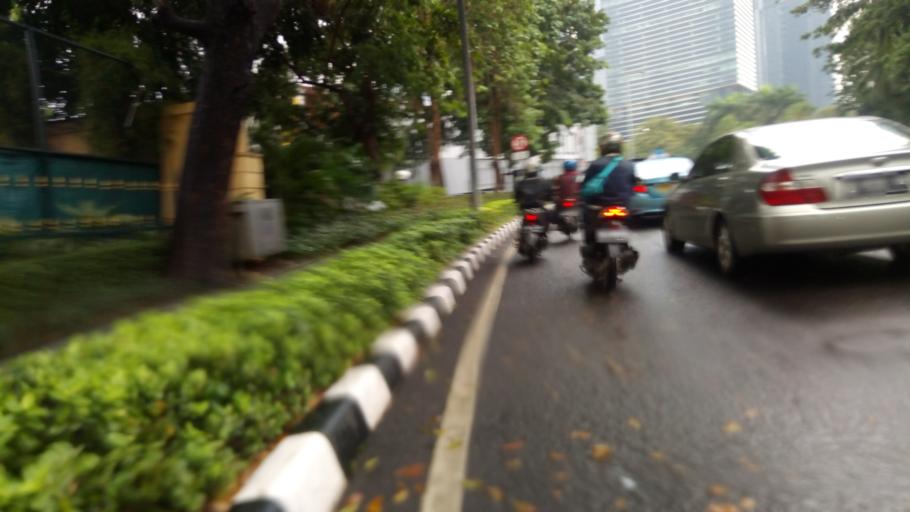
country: ID
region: Jakarta Raya
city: Jakarta
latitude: -6.2270
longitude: 106.8117
